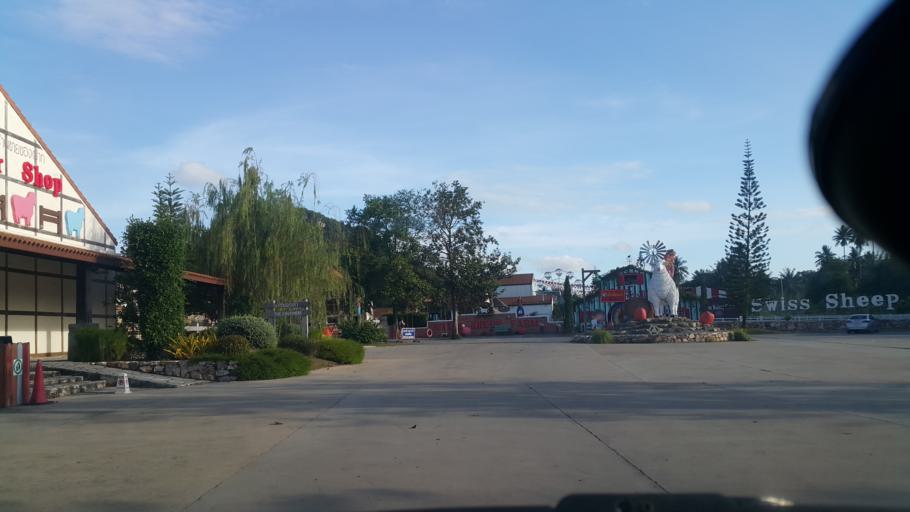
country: TH
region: Chon Buri
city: Sattahip
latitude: 12.7741
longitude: 100.9454
